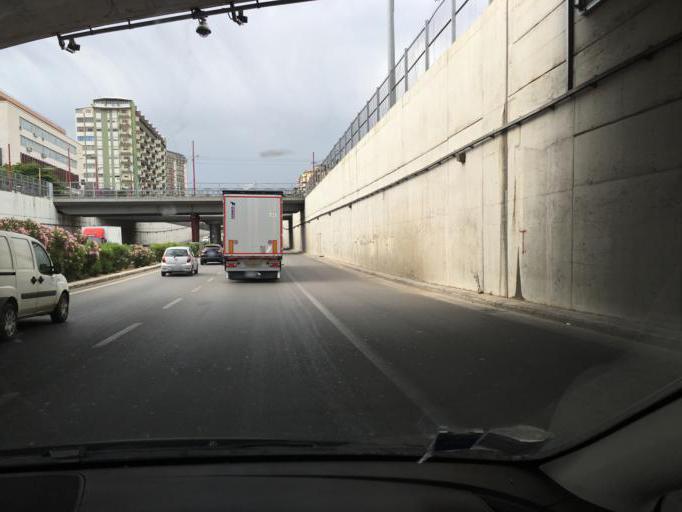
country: IT
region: Sicily
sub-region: Palermo
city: Palermo
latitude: 38.1296
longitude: 13.3298
